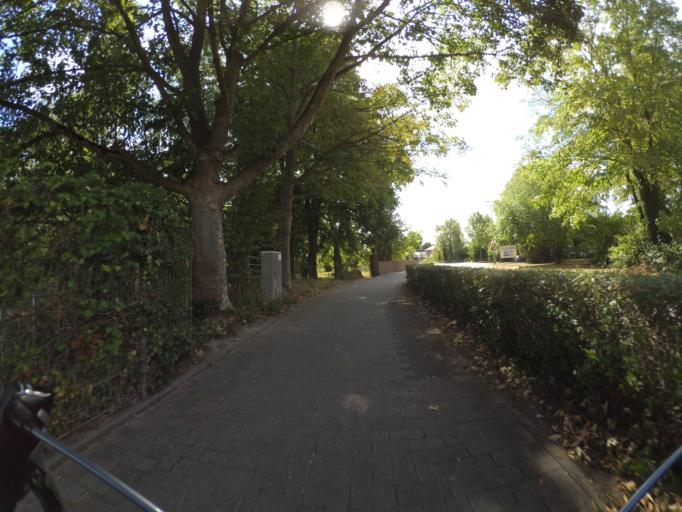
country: DE
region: North Rhine-Westphalia
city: Julich
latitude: 50.9003
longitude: 6.3517
